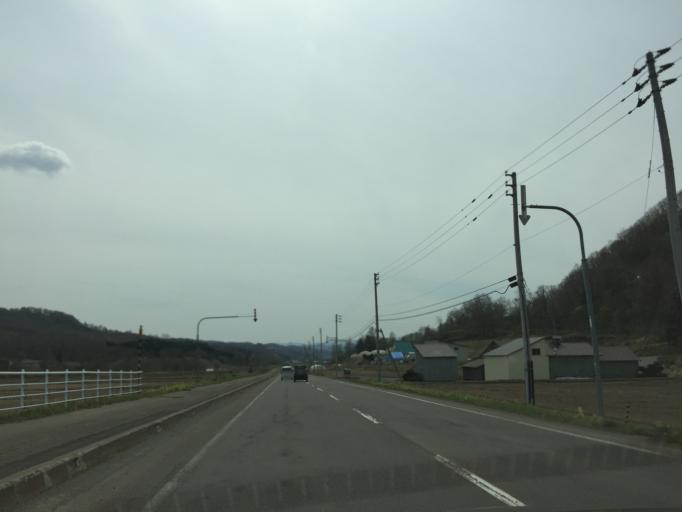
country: JP
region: Hokkaido
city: Ashibetsu
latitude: 43.5993
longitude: 142.2030
